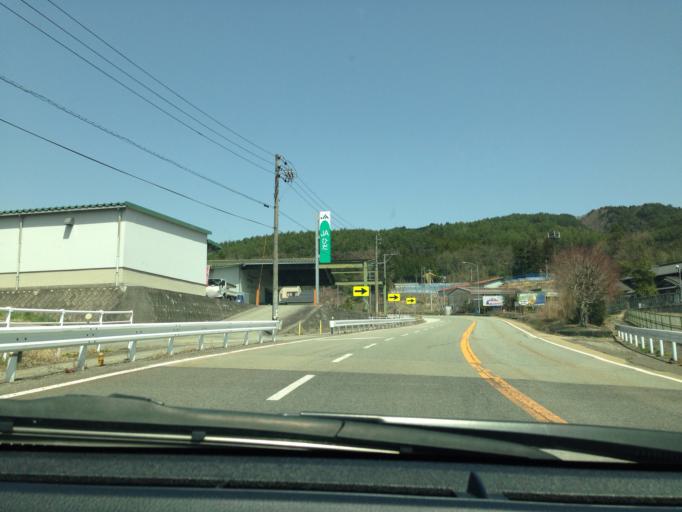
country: JP
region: Gifu
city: Takayama
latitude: 36.0767
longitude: 137.2673
